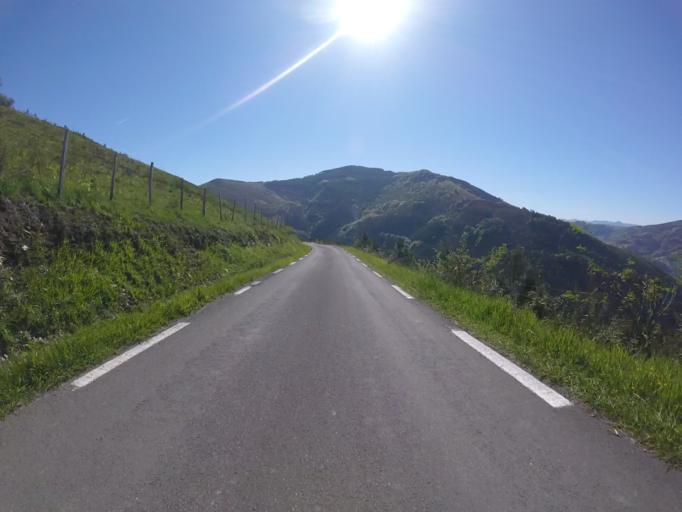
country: ES
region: Basque Country
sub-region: Provincia de Guipuzcoa
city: Errezil
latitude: 43.1886
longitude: -2.2054
